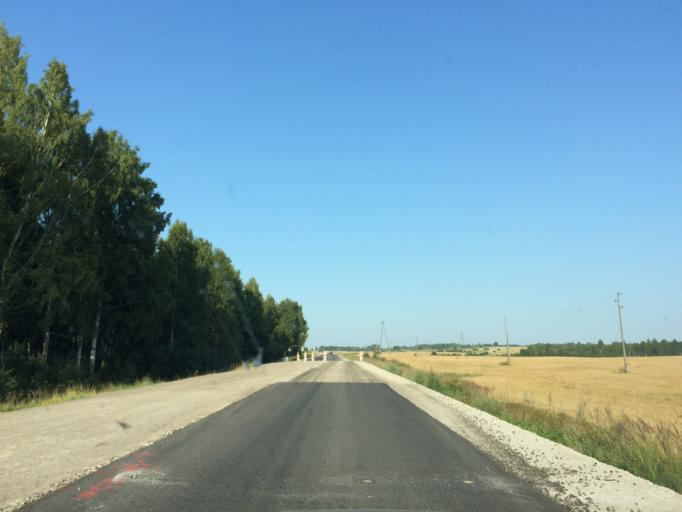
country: LV
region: Rezekne
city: Rezekne
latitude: 56.5175
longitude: 27.4996
